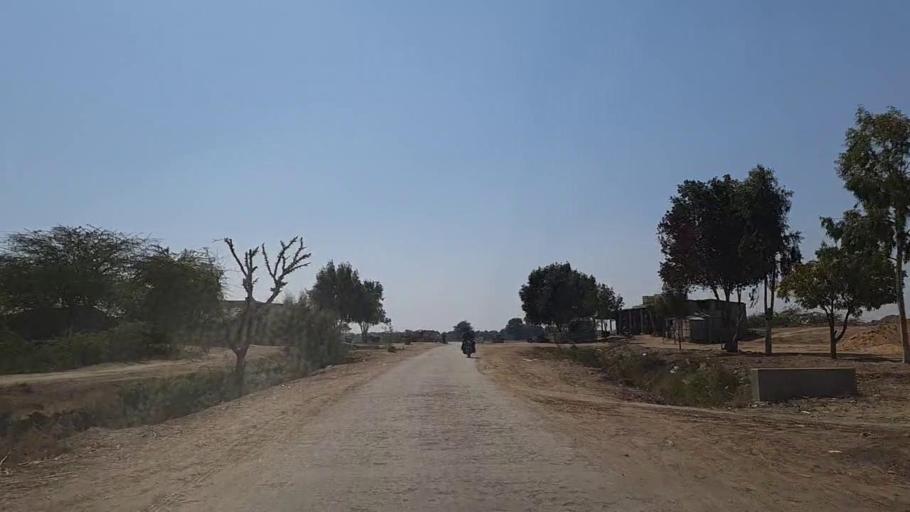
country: PK
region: Sindh
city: Samaro
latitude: 25.3488
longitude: 69.3129
